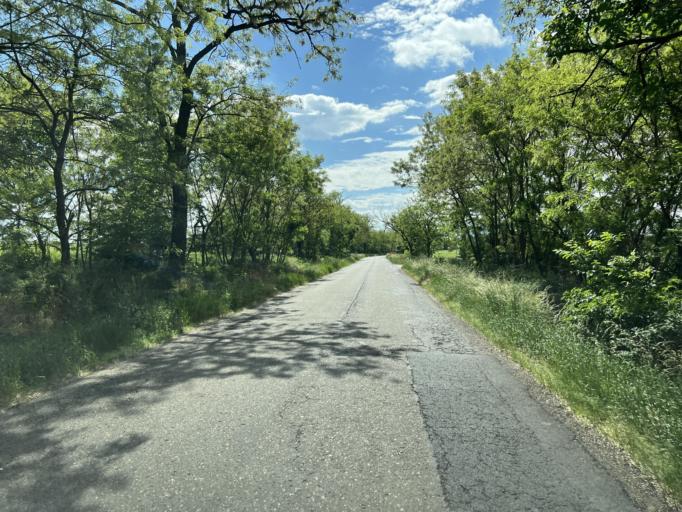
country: HU
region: Pest
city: Vacszentlaszlo
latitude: 47.5606
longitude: 19.5613
